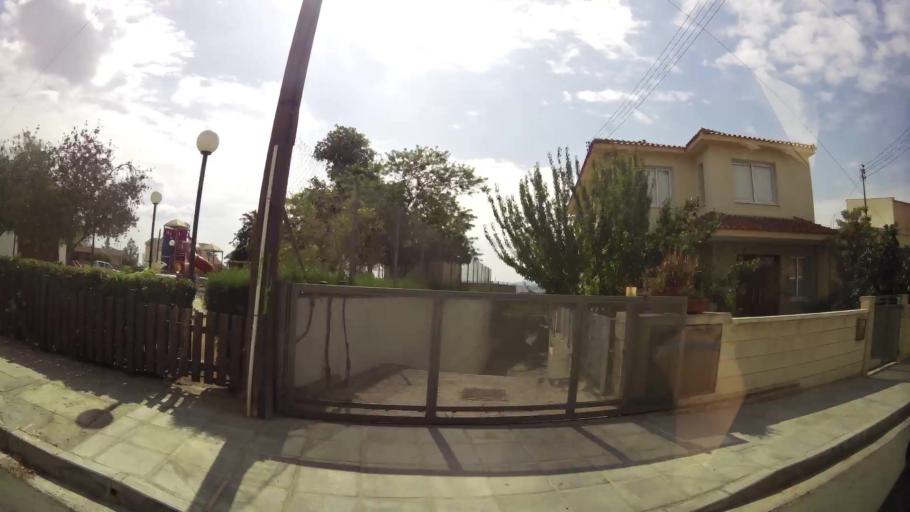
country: CY
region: Lefkosia
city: Tseri
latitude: 35.0723
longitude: 33.3319
